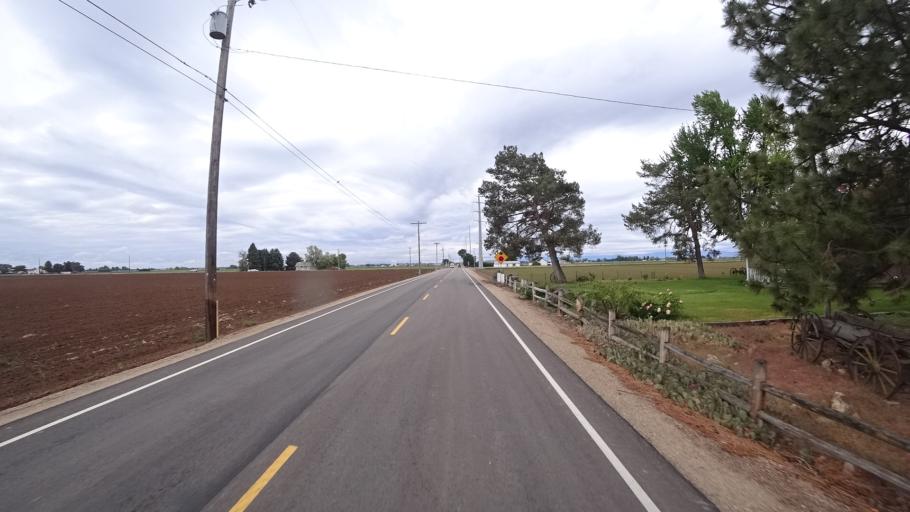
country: US
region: Idaho
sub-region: Ada County
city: Star
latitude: 43.6650
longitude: -116.5129
